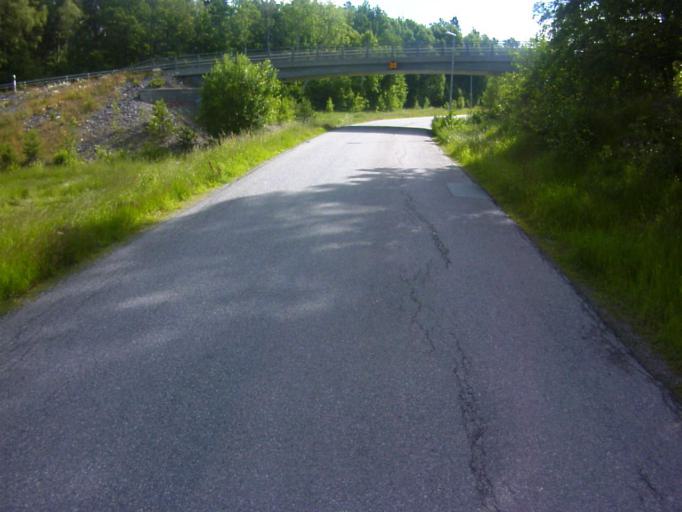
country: SE
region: Soedermanland
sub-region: Eskilstuna Kommun
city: Skogstorp
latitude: 59.3519
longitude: 16.4644
